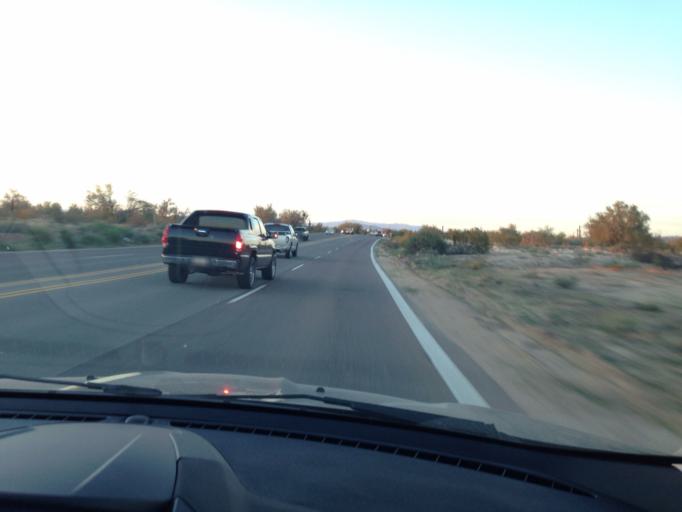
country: US
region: Arizona
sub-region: Maricopa County
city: Cave Creek
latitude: 33.7114
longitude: -111.9741
